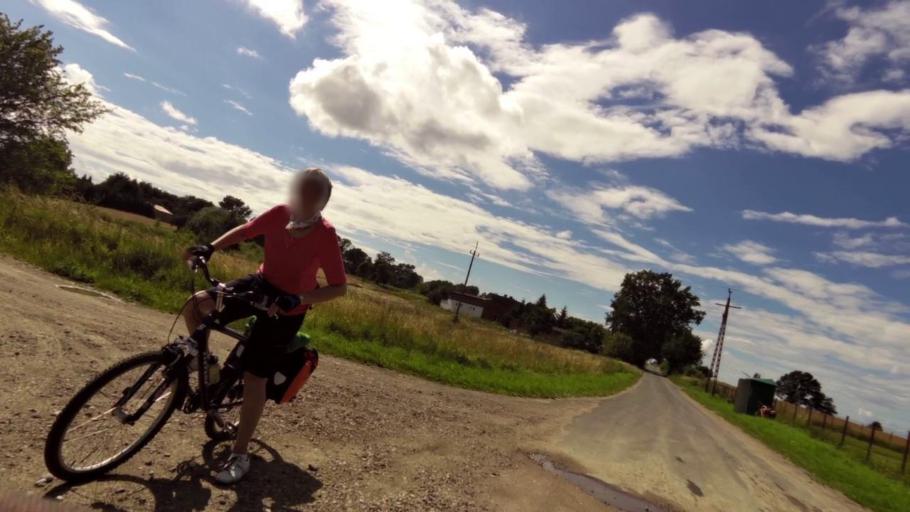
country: PL
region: West Pomeranian Voivodeship
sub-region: Powiat slawienski
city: Slawno
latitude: 54.5115
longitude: 16.7064
